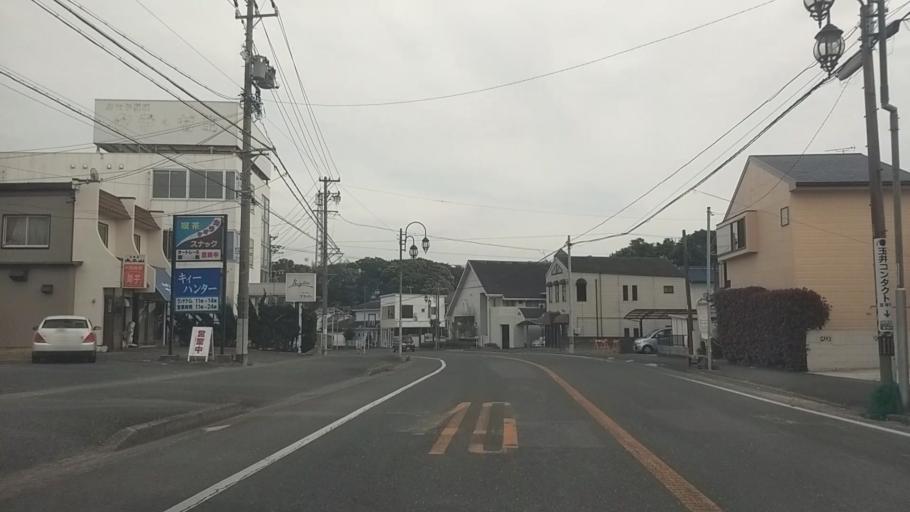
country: JP
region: Shizuoka
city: Hamamatsu
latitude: 34.7287
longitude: 137.6906
